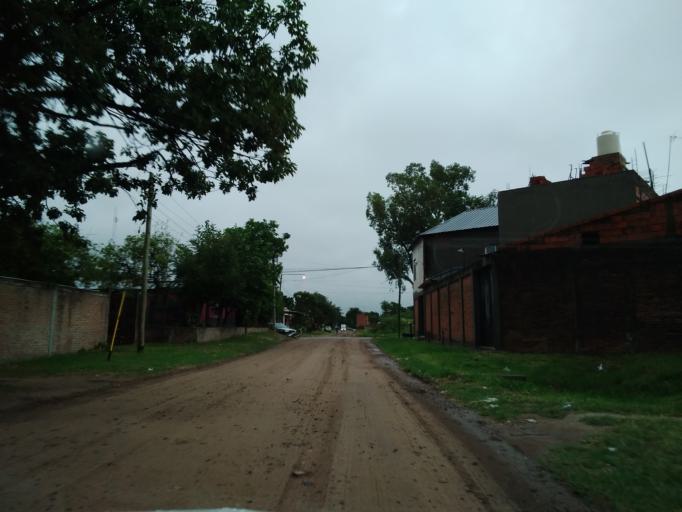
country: AR
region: Corrientes
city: Corrientes
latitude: -27.4850
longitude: -58.8230
